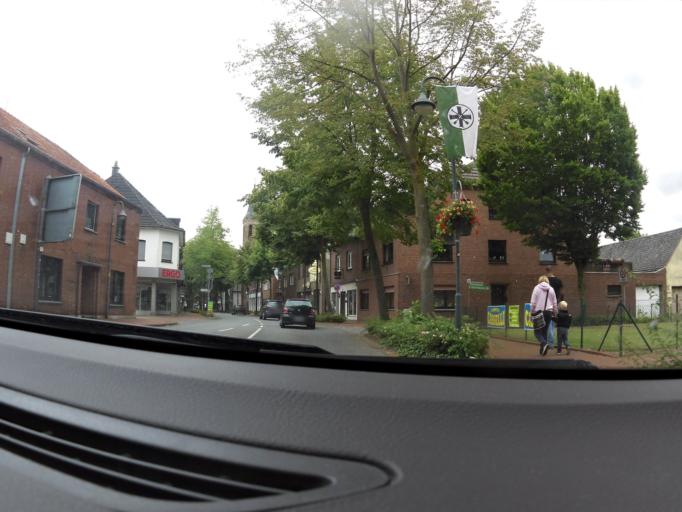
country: DE
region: North Rhine-Westphalia
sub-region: Regierungsbezirk Dusseldorf
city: Sonsbeck
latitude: 51.6114
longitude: 6.3758
